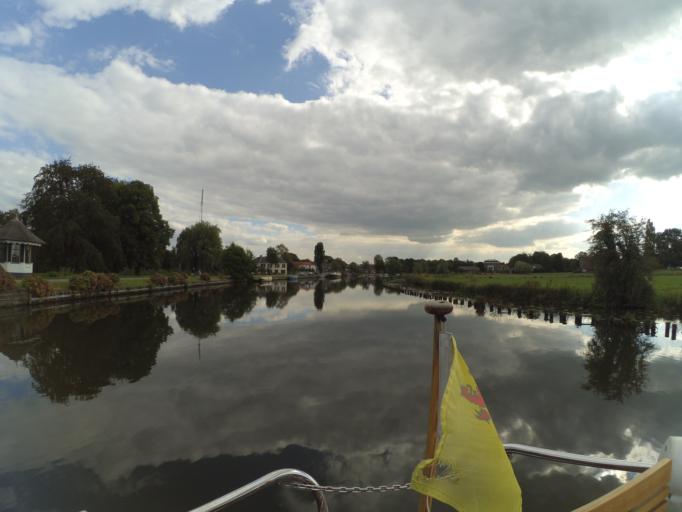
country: NL
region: Utrecht
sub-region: Stichtse Vecht
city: Maarssen
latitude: 52.1527
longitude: 5.0343
